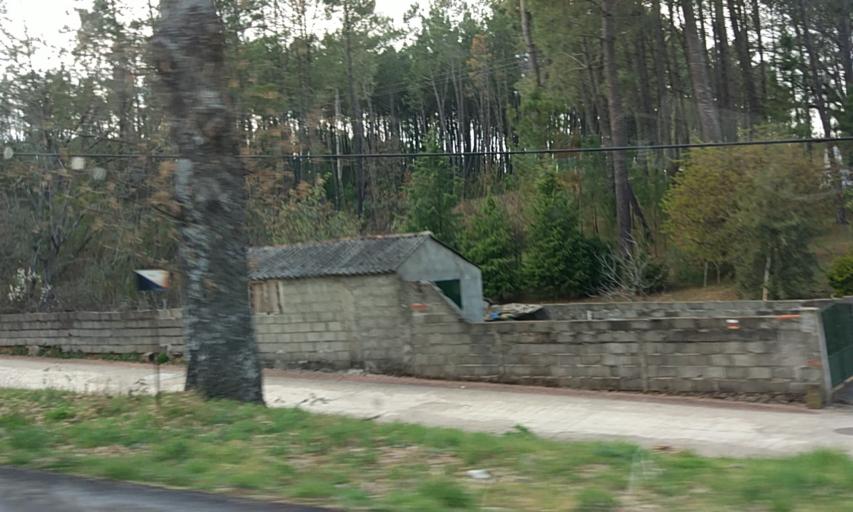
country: ES
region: Castille and Leon
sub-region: Provincia de Salamanca
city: Villasrubias
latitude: 40.3405
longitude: -6.6398
